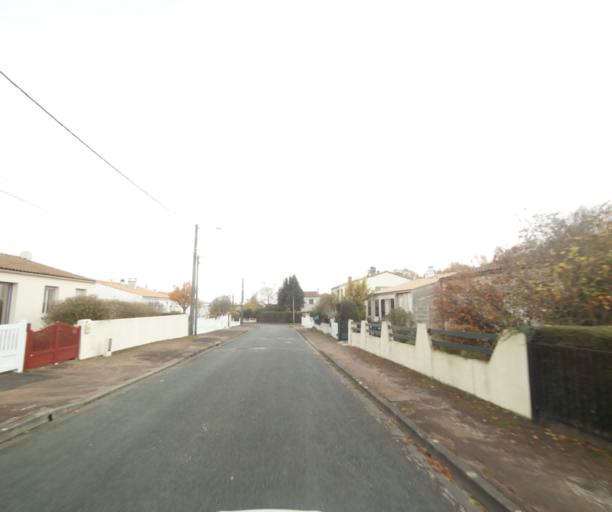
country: FR
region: Poitou-Charentes
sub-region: Departement de la Charente-Maritime
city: Saintes
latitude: 45.7316
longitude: -0.6514
